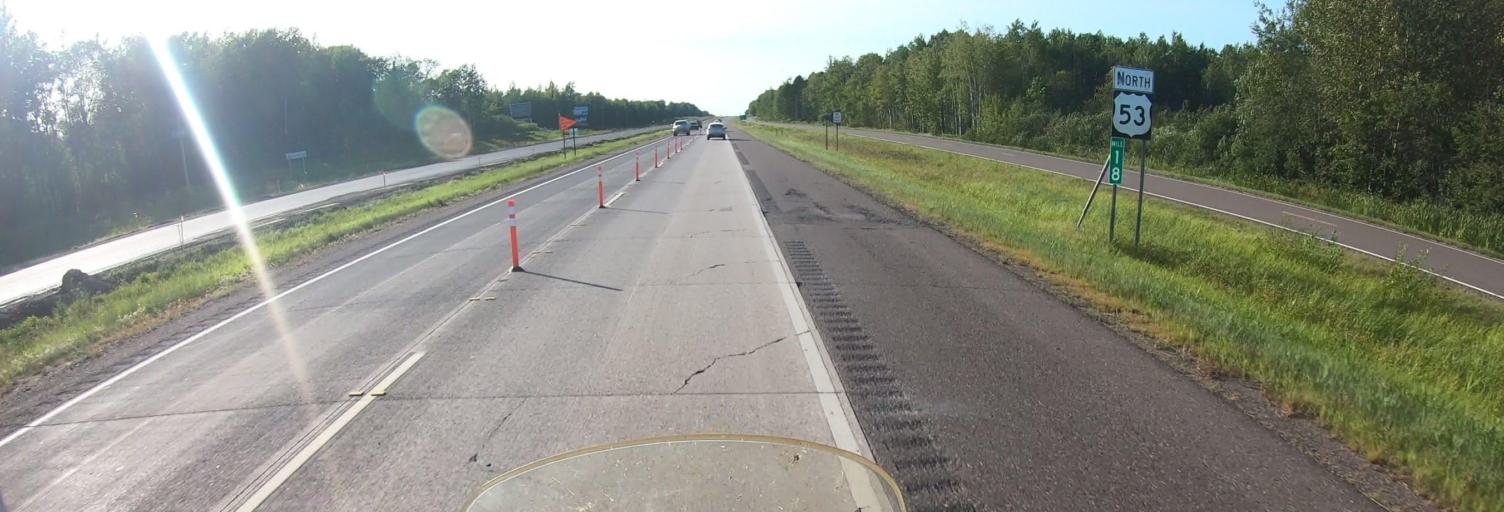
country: US
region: Minnesota
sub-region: Saint Louis County
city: Hermantown
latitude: 46.8956
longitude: -92.3662
